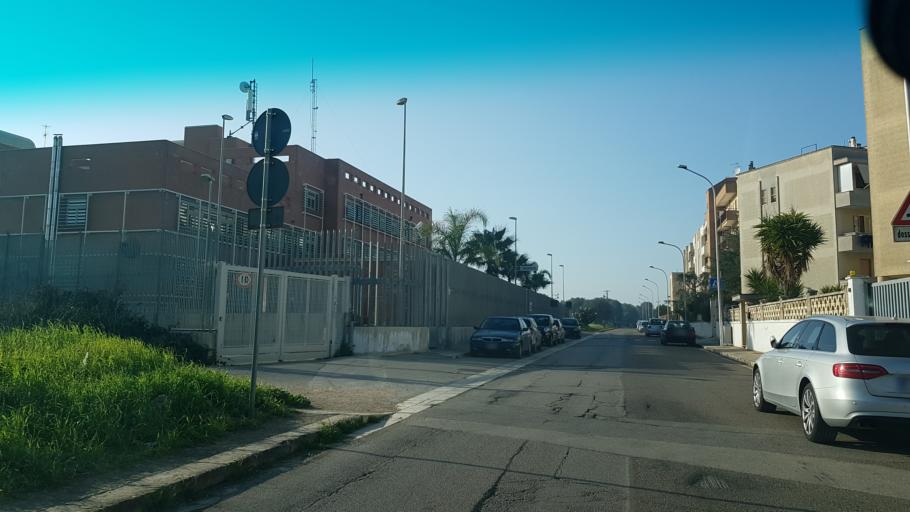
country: IT
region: Apulia
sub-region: Provincia di Brindisi
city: San Vito dei Normanni
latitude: 40.6626
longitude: 17.6956
